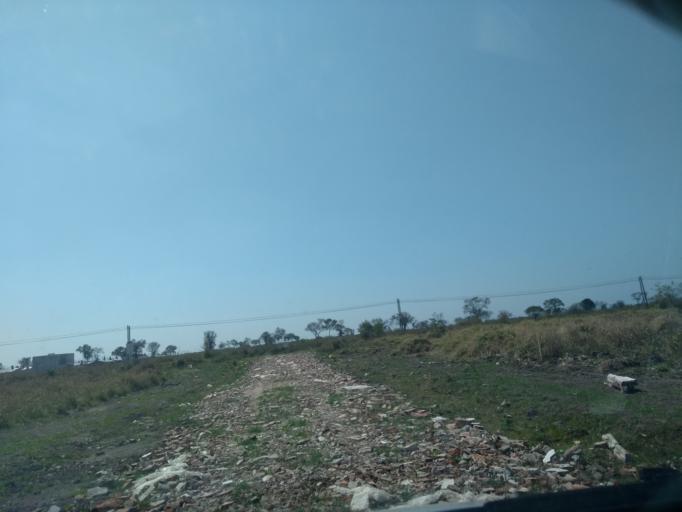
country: AR
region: Chaco
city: Resistencia
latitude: -27.4092
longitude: -58.9632
